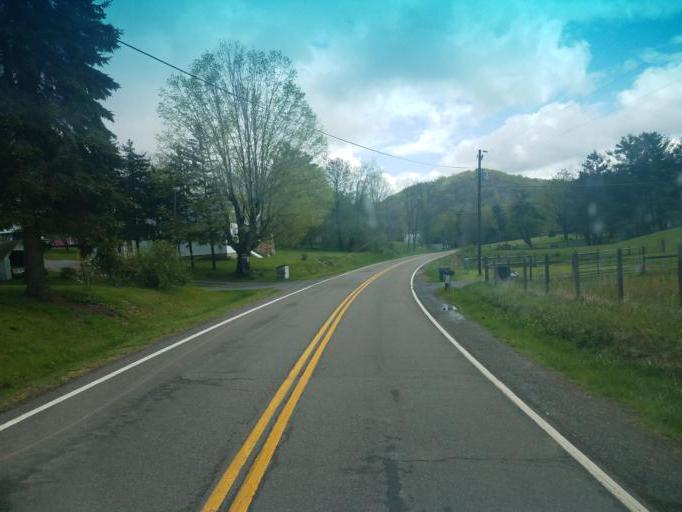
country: US
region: Virginia
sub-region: Wythe County
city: Rural Retreat
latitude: 37.0172
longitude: -81.3484
